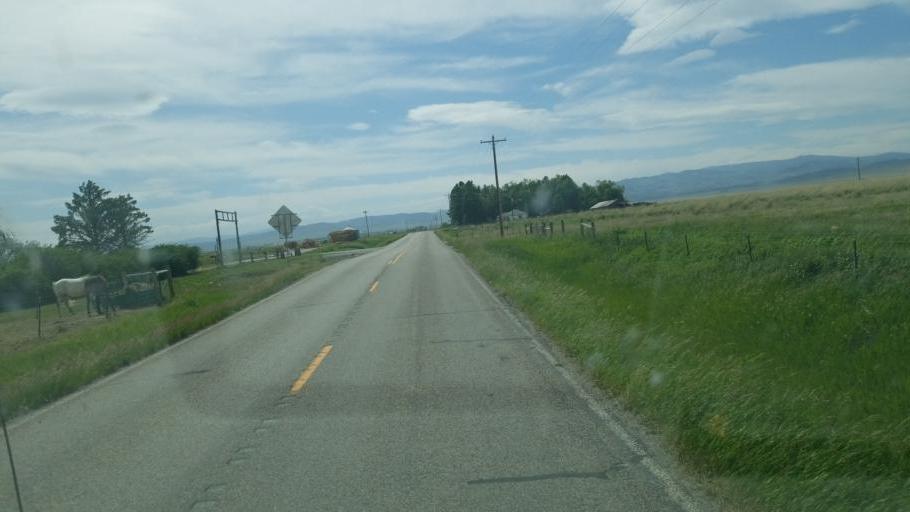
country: US
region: Montana
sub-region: Broadwater County
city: Townsend
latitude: 46.1736
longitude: -111.4694
